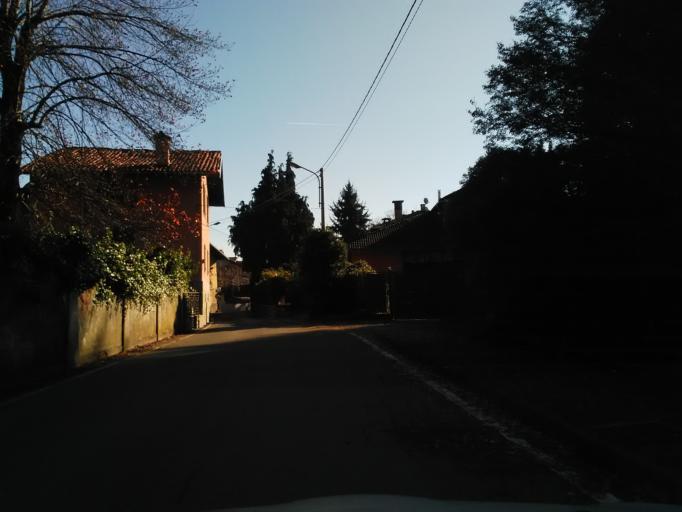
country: IT
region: Piedmont
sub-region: Provincia di Vercelli
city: Borgosesia
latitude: 45.7355
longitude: 8.2727
